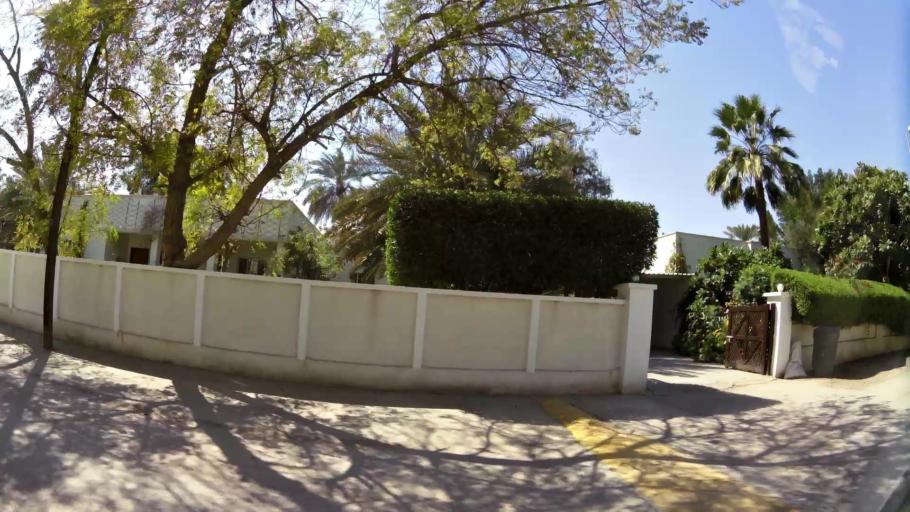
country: BH
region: Manama
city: Manama
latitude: 26.2156
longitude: 50.5833
